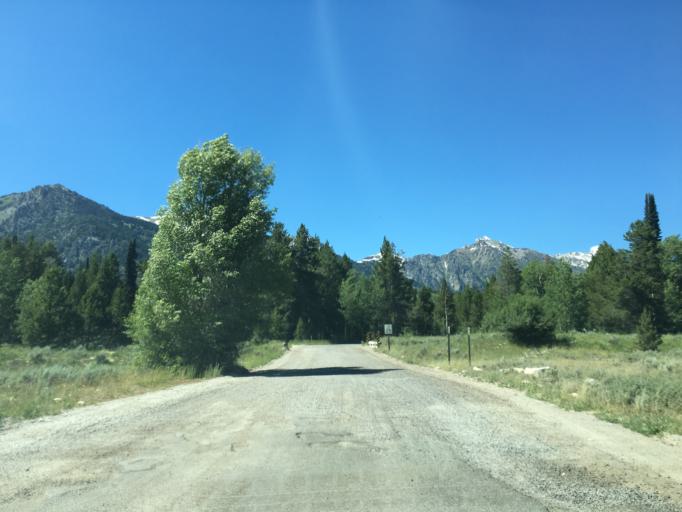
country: US
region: Wyoming
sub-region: Teton County
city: Moose Wilson Road
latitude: 43.6043
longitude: -110.7932
